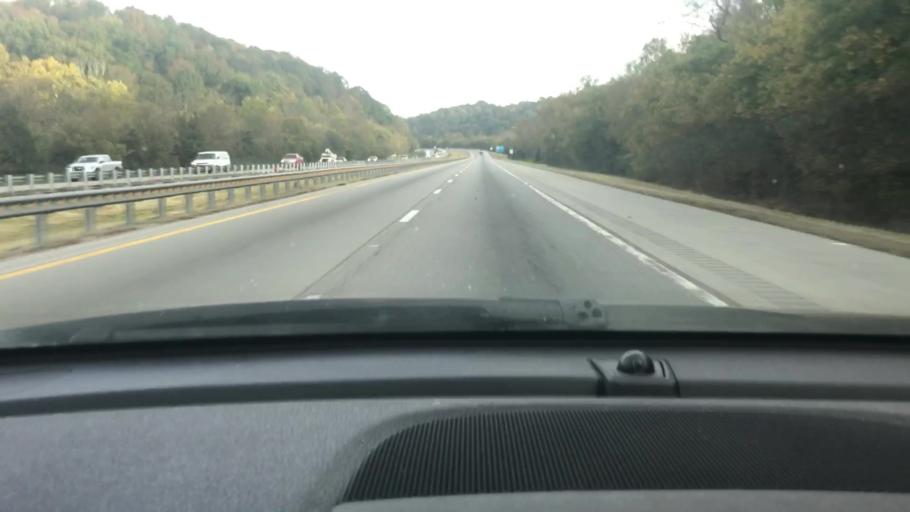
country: US
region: Tennessee
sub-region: Sumner County
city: Millersville
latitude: 36.3918
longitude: -86.7160
